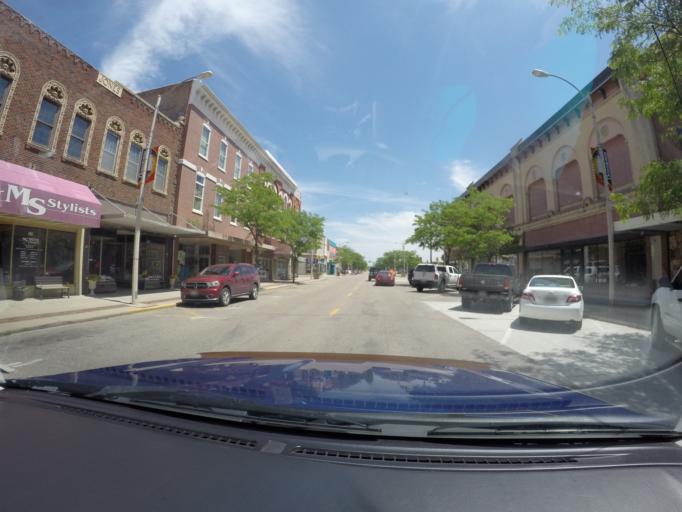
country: US
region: Nebraska
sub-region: Hall County
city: Grand Island
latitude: 40.9256
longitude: -98.3406
